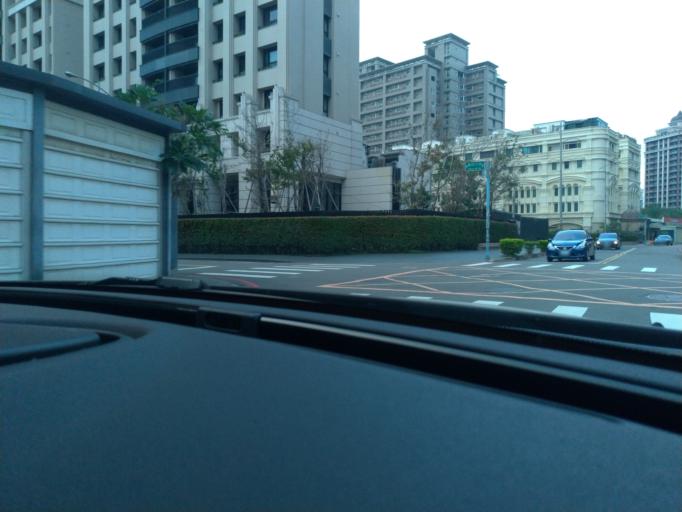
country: TW
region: Taiwan
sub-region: Hsinchu
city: Zhubei
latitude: 24.8019
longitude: 121.0352
